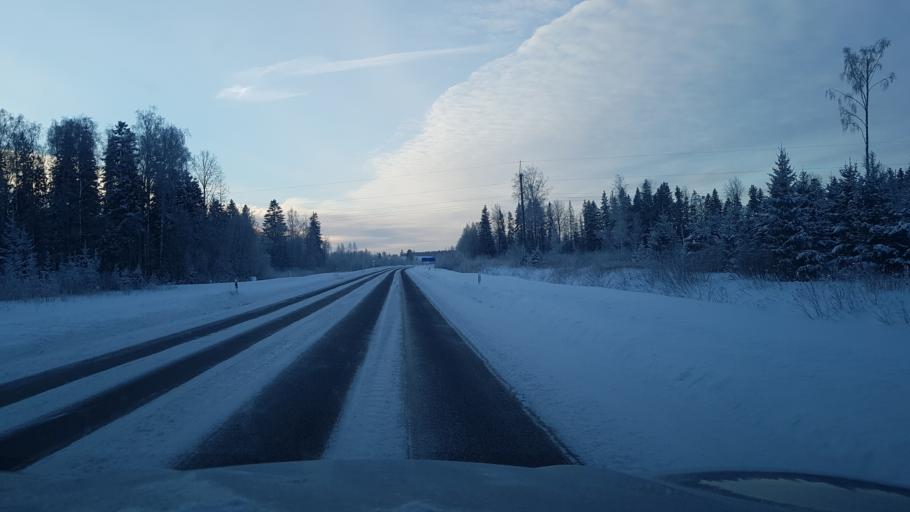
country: EE
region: Ida-Virumaa
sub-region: Johvi vald
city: Johvi
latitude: 59.3436
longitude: 27.4679
